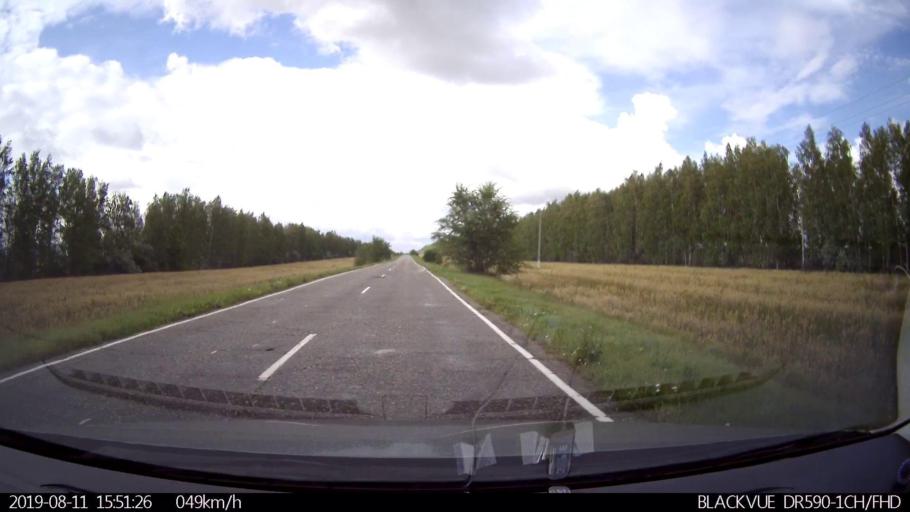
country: RU
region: Ulyanovsk
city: Ignatovka
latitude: 53.9187
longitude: 47.6560
